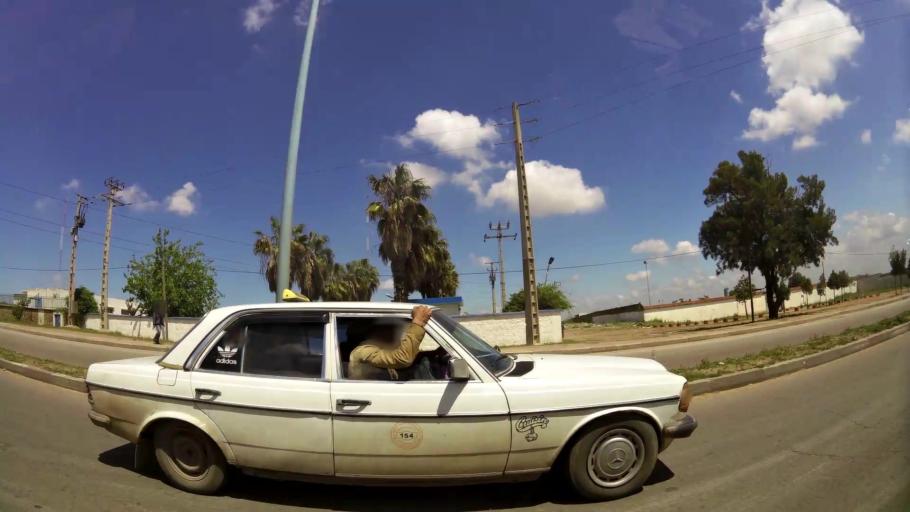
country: MA
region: Grand Casablanca
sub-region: Casablanca
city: Casablanca
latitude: 33.5320
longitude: -7.5702
